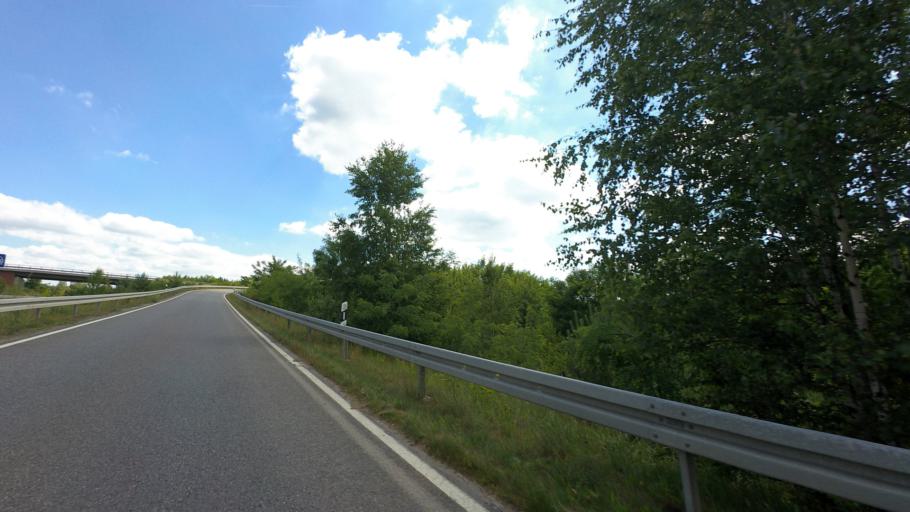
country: DE
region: Brandenburg
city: Senftenberg
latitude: 51.5295
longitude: 14.0149
